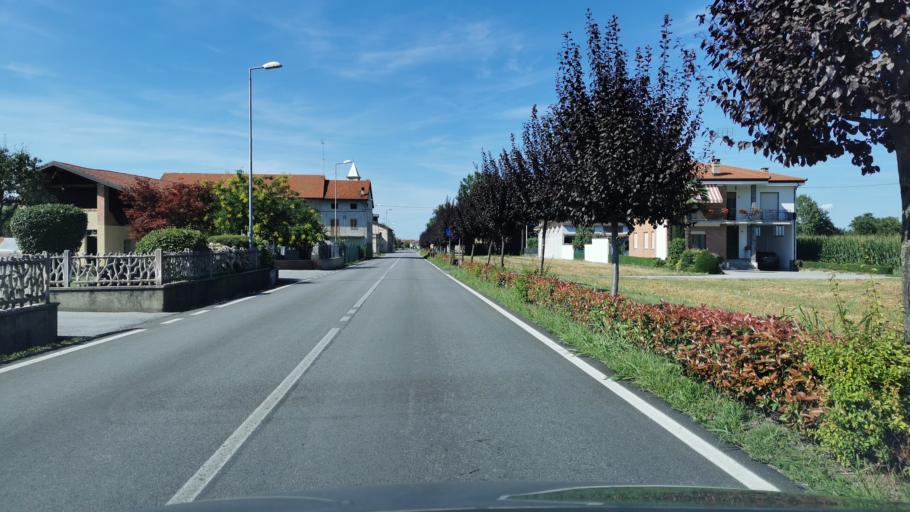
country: IT
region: Piedmont
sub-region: Provincia di Cuneo
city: Boves
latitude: 44.3417
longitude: 7.5575
